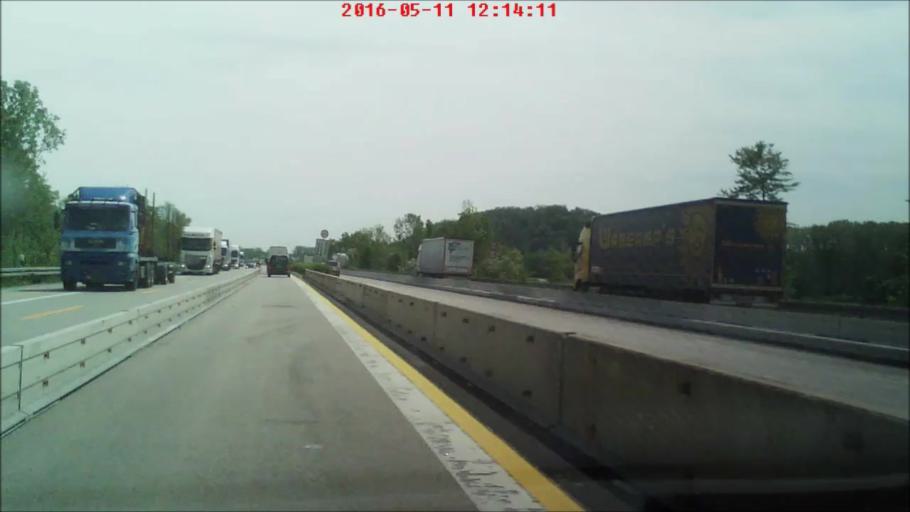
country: DE
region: Bavaria
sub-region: Lower Bavaria
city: Metten
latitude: 48.8369
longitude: 12.9027
